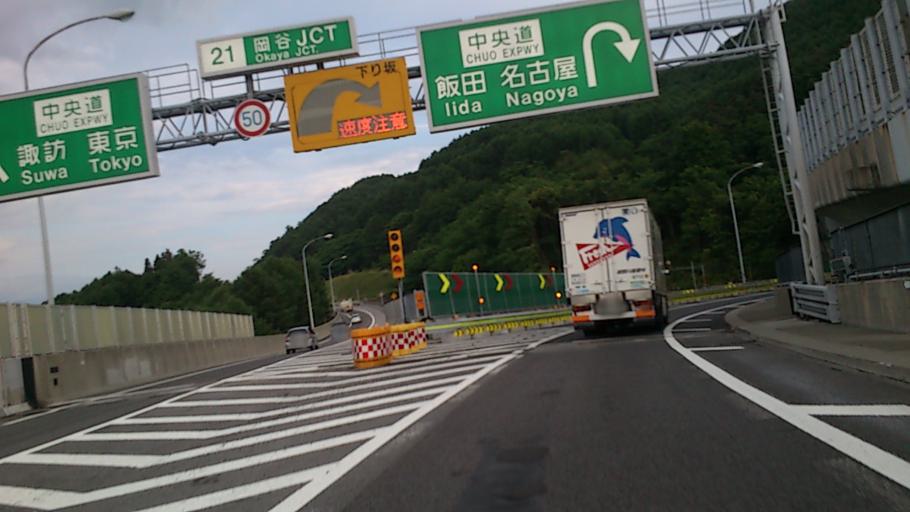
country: JP
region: Nagano
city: Okaya
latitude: 36.0540
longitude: 138.0432
